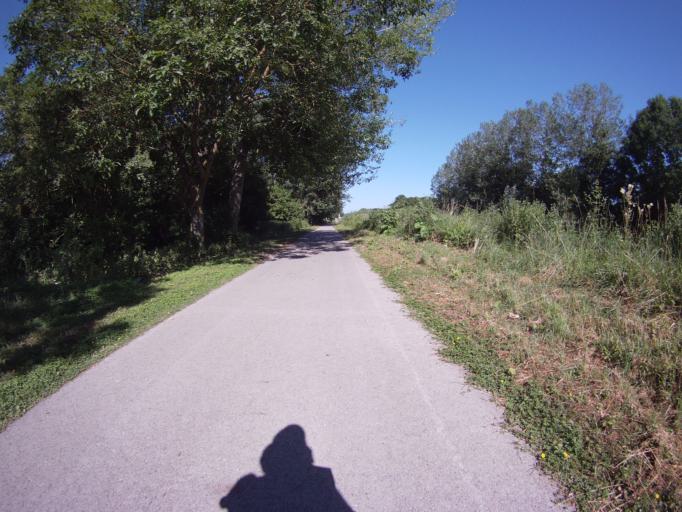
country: FR
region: Champagne-Ardenne
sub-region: Departement de la Marne
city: Ay
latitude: 49.0531
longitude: 3.9955
